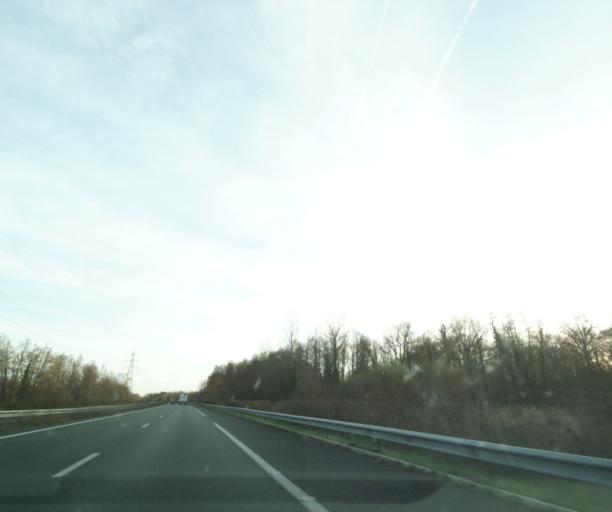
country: FR
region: Aquitaine
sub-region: Departement de la Gironde
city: Saint-Christoly-de-Blaye
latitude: 45.1250
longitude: -0.4858
